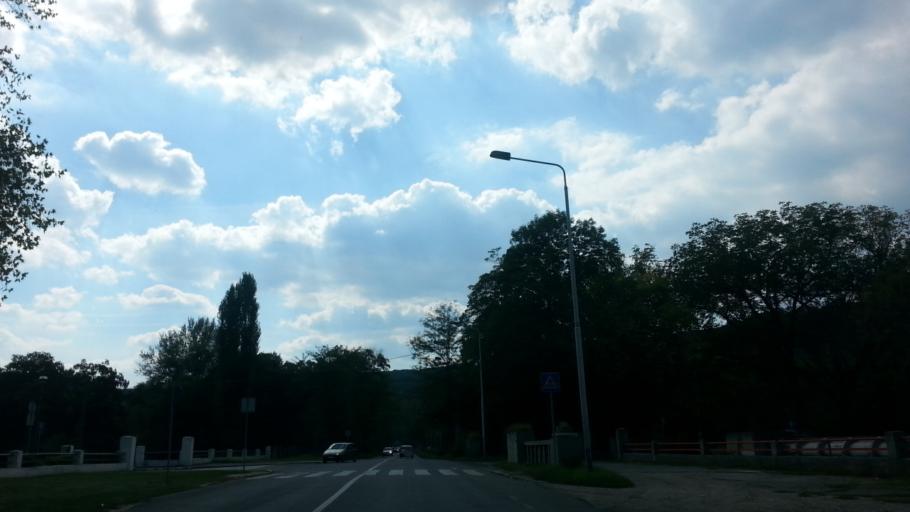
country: RS
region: Central Serbia
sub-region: Belgrade
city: Savski Venac
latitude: 44.7768
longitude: 20.4402
